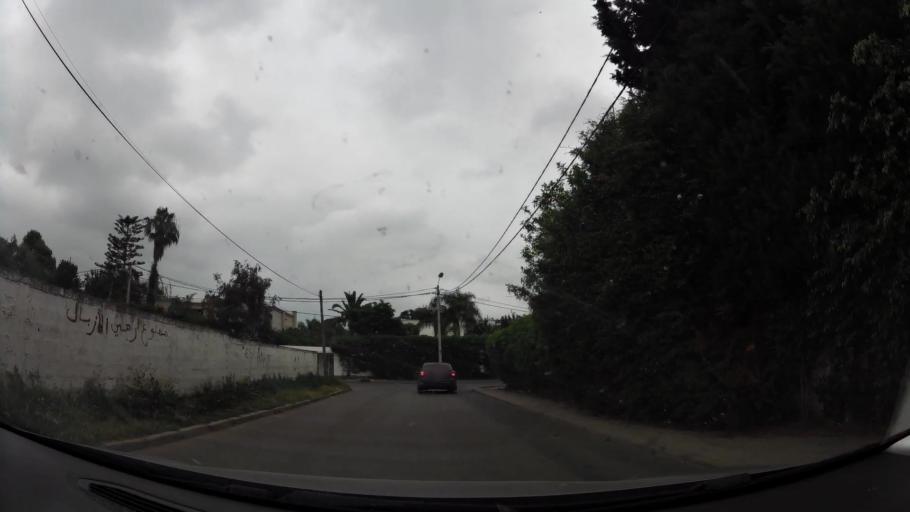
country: MA
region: Rabat-Sale-Zemmour-Zaer
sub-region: Rabat
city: Rabat
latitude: 33.9759
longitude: -6.8280
